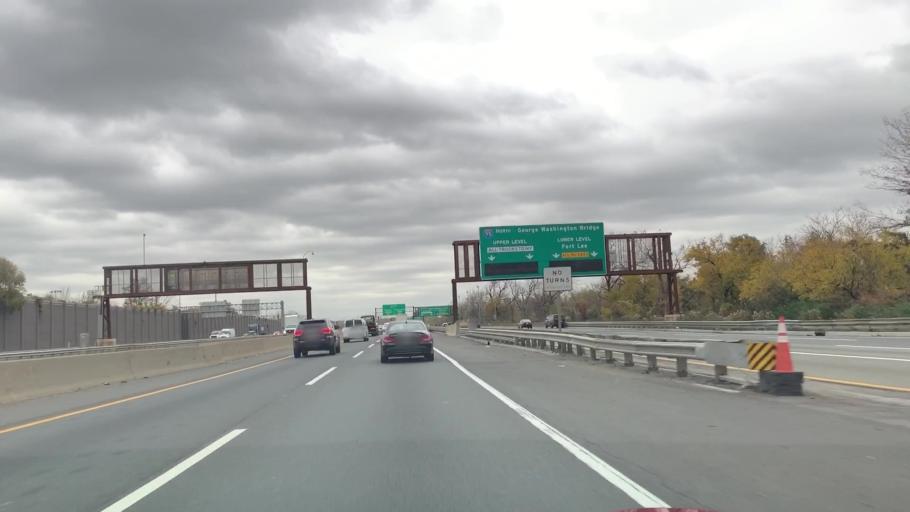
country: US
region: New Jersey
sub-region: Bergen County
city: Ridgefield Park
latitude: 40.8540
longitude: -74.0141
